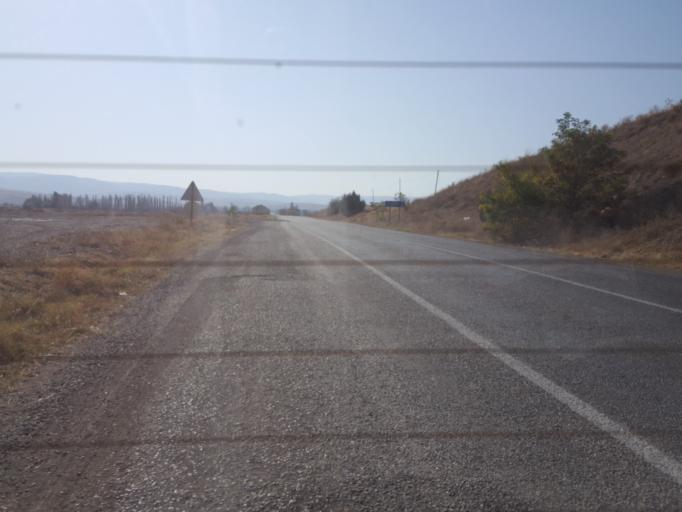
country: TR
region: Corum
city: Iskilip
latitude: 40.6136
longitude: 34.5770
